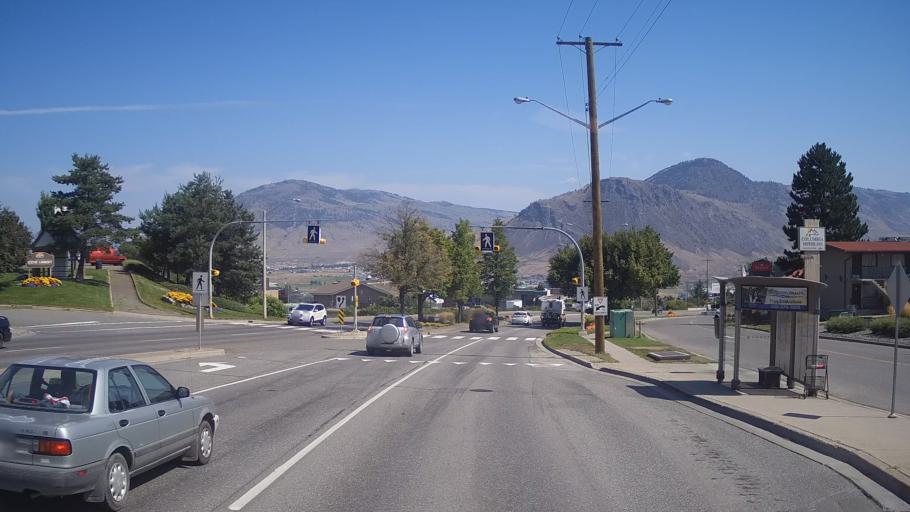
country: CA
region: British Columbia
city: Kamloops
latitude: 50.6722
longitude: -120.3537
